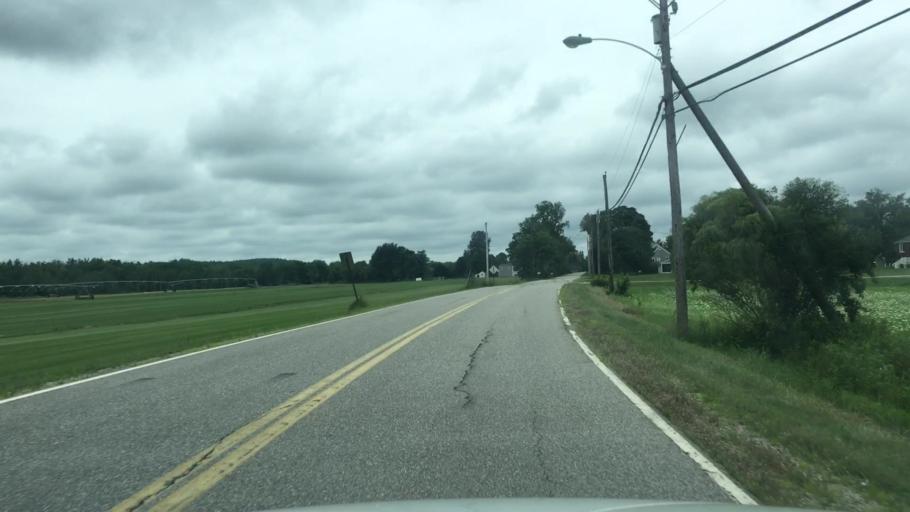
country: US
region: Maine
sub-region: York County
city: Biddeford
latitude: 43.5034
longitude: -70.4882
